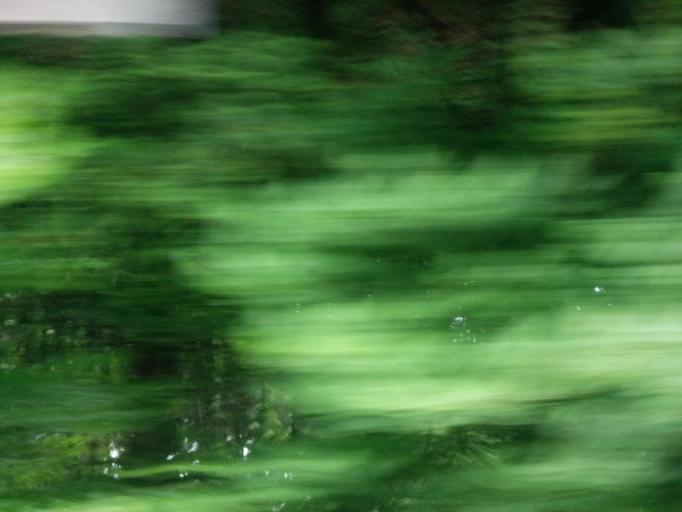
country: JP
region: Tochigi
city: Imaichi
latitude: 36.6487
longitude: 139.7239
